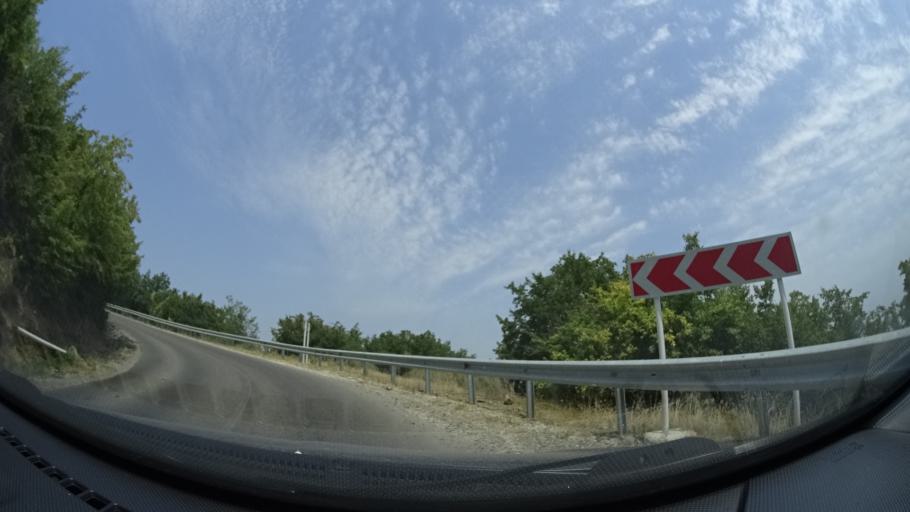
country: GE
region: Kakheti
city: Sighnaghi
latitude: 41.6233
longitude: 45.9314
